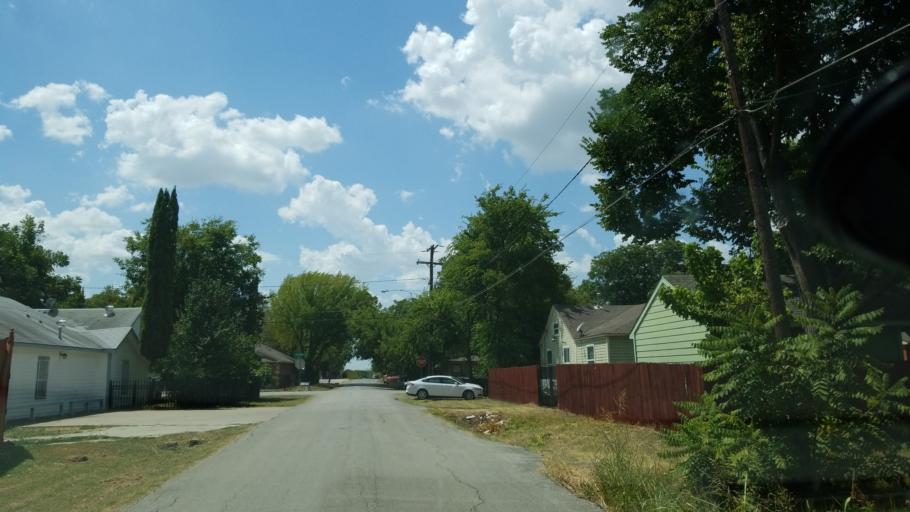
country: US
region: Texas
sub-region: Dallas County
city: Cockrell Hill
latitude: 32.7469
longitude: -96.9069
